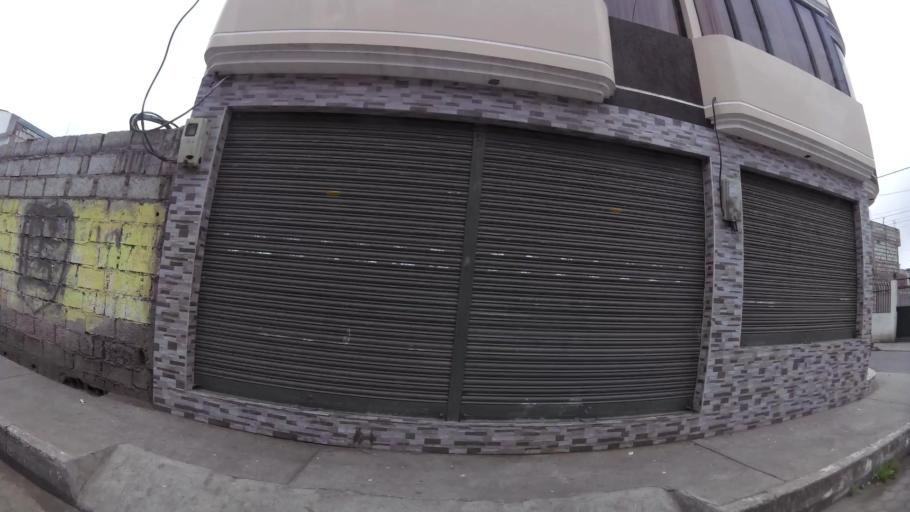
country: EC
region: Cotopaxi
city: San Miguel de Salcedo
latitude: -1.0419
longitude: -78.5856
